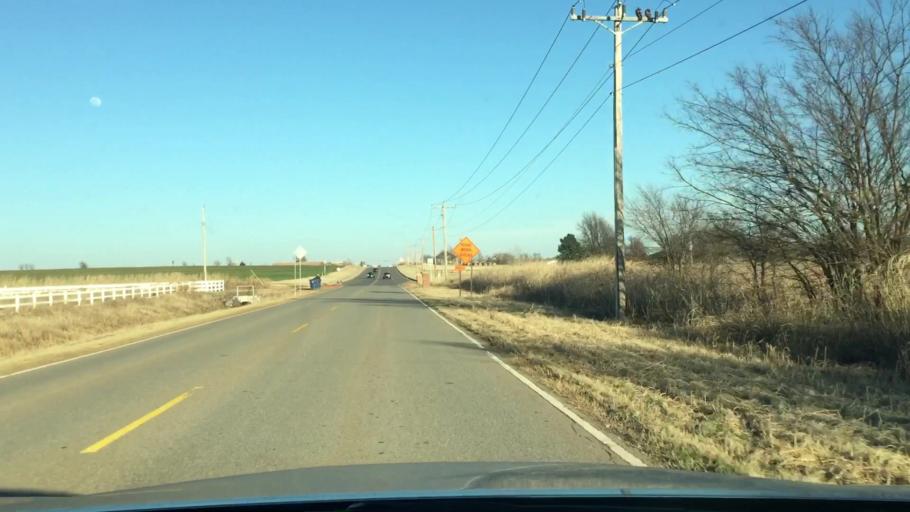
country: US
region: Oklahoma
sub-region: Oklahoma County
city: The Village
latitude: 35.6531
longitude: -97.5951
